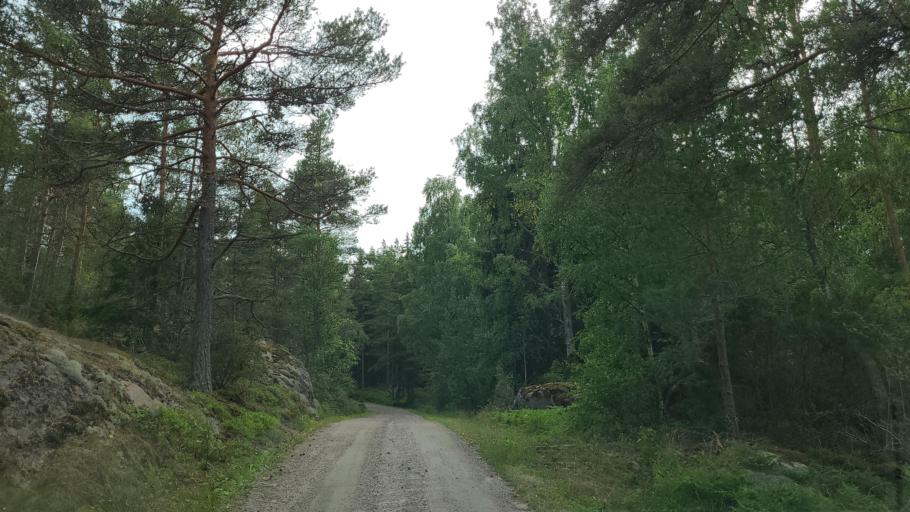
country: FI
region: Varsinais-Suomi
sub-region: Aboland-Turunmaa
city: Nagu
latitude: 60.1389
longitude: 21.8020
